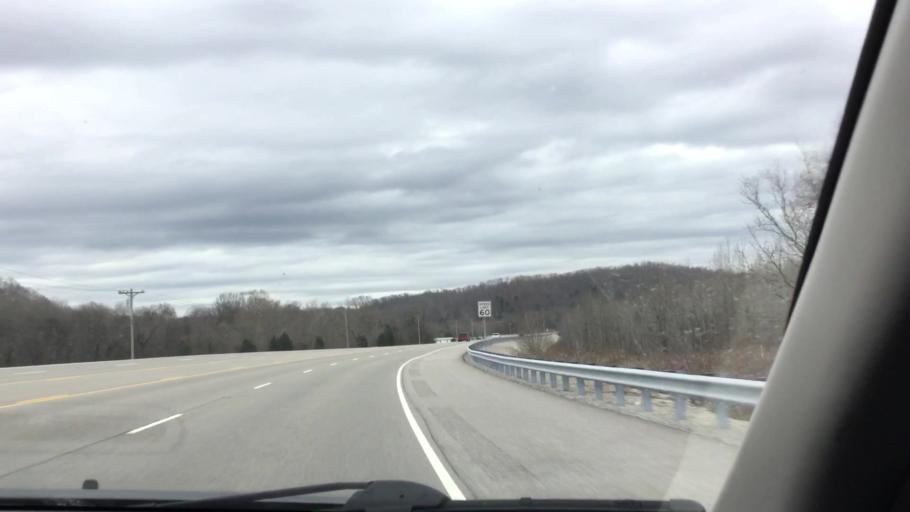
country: US
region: Tennessee
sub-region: Lewis County
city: Hohenwald
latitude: 35.5752
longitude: -87.4279
